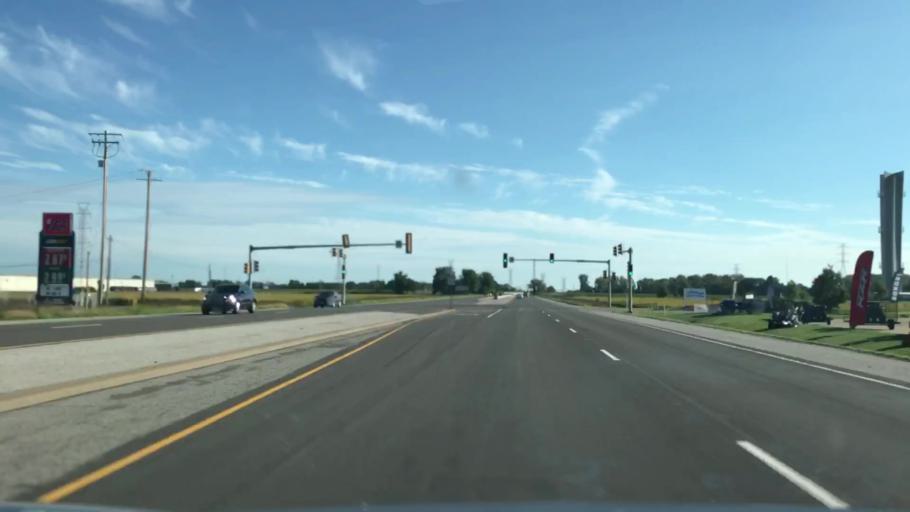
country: US
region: Illinois
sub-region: Madison County
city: Hartford
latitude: 38.8144
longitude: -90.0987
